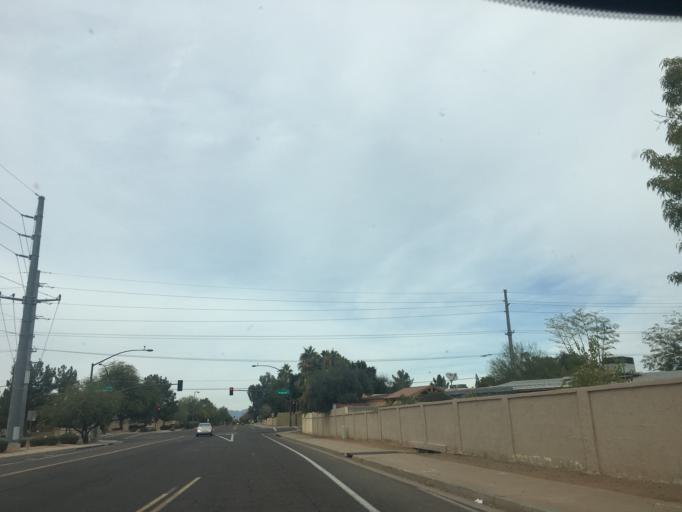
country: US
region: Arizona
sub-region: Maricopa County
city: Gilbert
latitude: 33.3636
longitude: -111.7984
